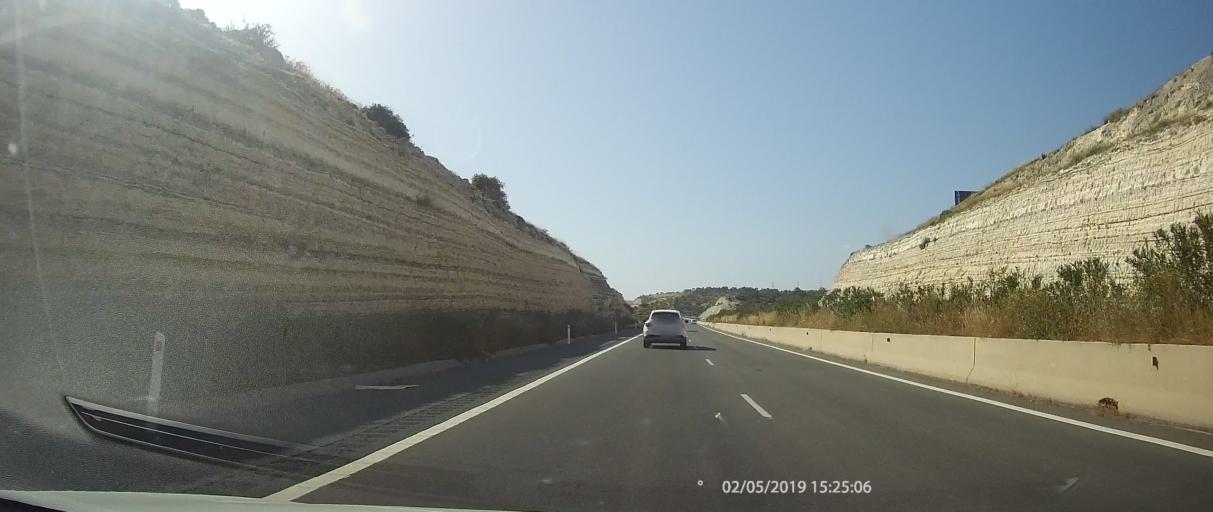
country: CY
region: Limassol
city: Sotira
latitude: 34.6860
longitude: 32.8761
